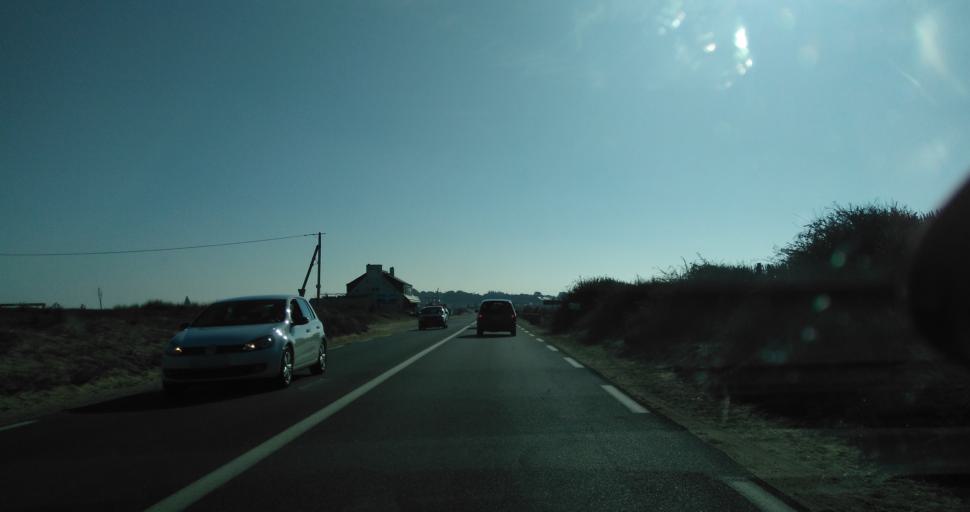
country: FR
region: Brittany
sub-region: Departement du Morbihan
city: Saint-Pierre-Quiberon
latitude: 47.5493
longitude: -3.1341
